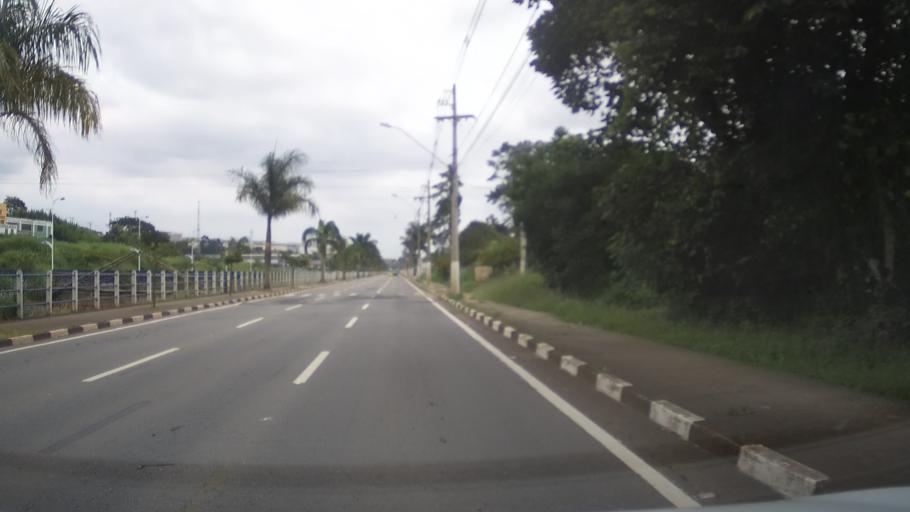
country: BR
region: Sao Paulo
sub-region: Aruja
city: Aruja
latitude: -23.3997
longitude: -46.3422
